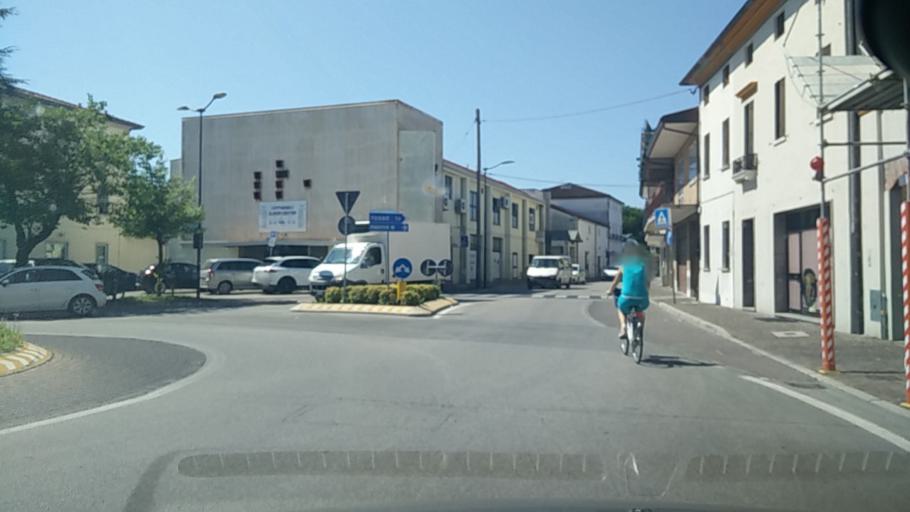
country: IT
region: Veneto
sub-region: Provincia di Venezia
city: Camponogara
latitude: 45.3839
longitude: 12.0722
